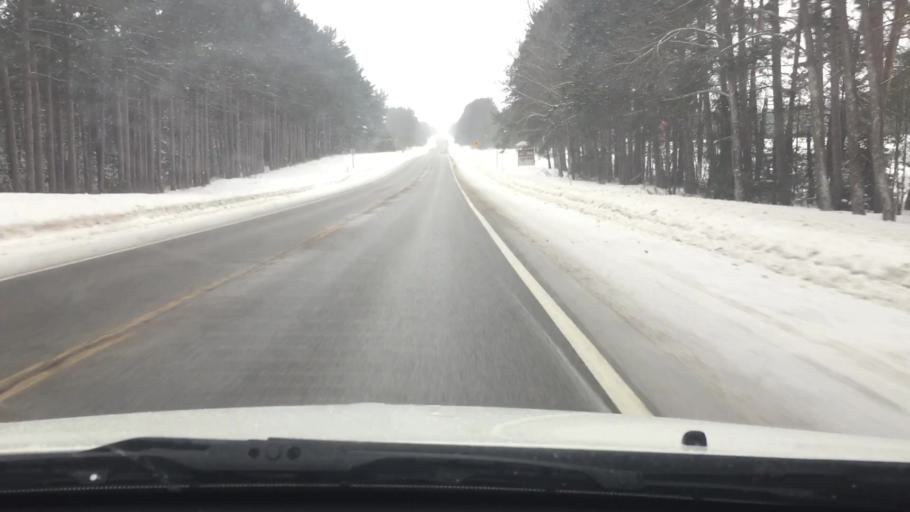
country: US
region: Michigan
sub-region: Otsego County
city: Gaylord
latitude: 45.0619
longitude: -84.8123
